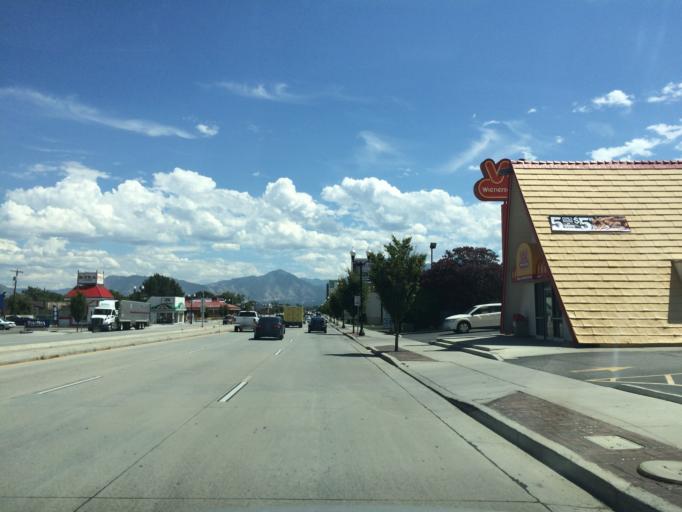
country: US
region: Utah
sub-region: Salt Lake County
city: West Valley City
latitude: 40.6965
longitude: -111.9666
